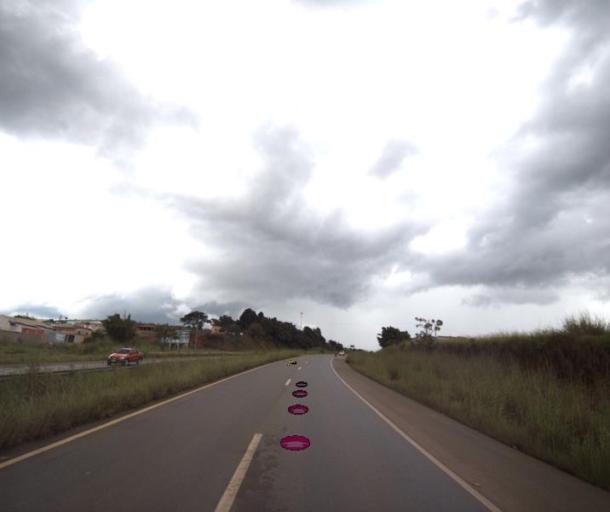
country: BR
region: Goias
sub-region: Anapolis
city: Anapolis
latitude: -16.2684
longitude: -48.9789
